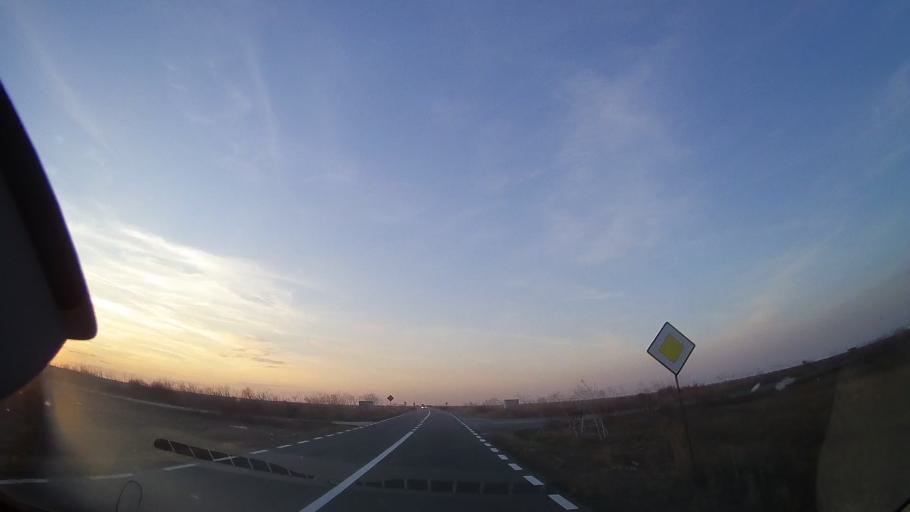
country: RO
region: Constanta
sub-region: Comuna Topraisar
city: Topraisar
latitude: 44.0184
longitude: 28.4252
